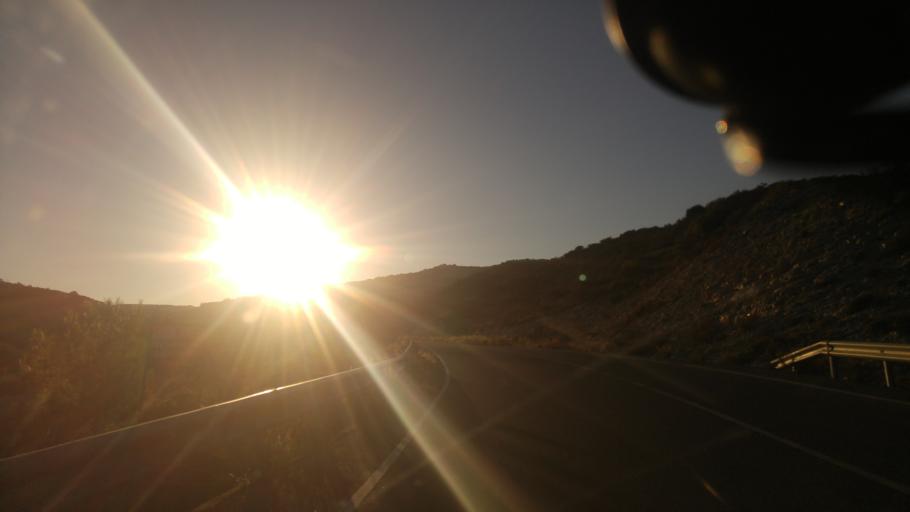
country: CY
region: Limassol
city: Pachna
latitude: 34.8634
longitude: 32.8133
